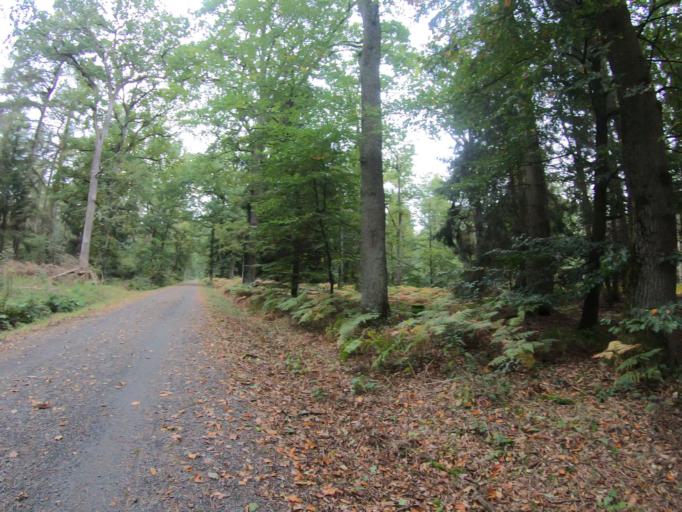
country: DE
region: Lower Saxony
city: Gifhorn
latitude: 52.4569
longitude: 10.5625
